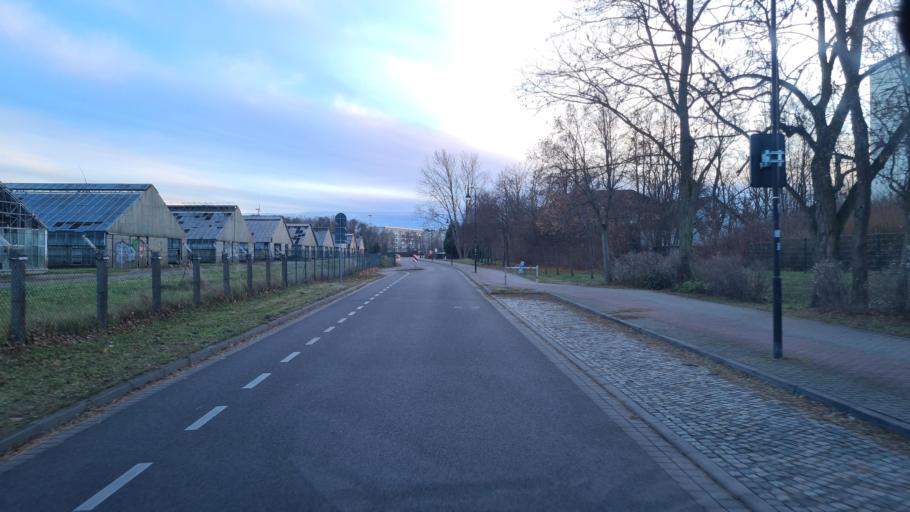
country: DE
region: Brandenburg
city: Vetschau
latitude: 51.7811
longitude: 14.0866
